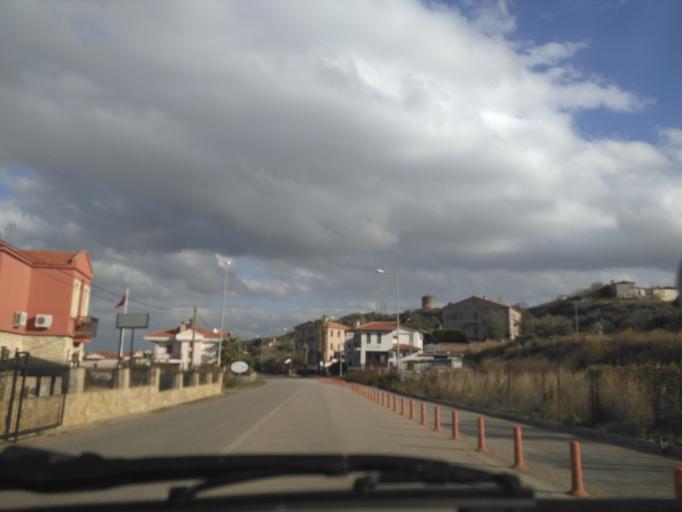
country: TR
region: Balikesir
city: Ayvalik
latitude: 39.3372
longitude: 26.6592
